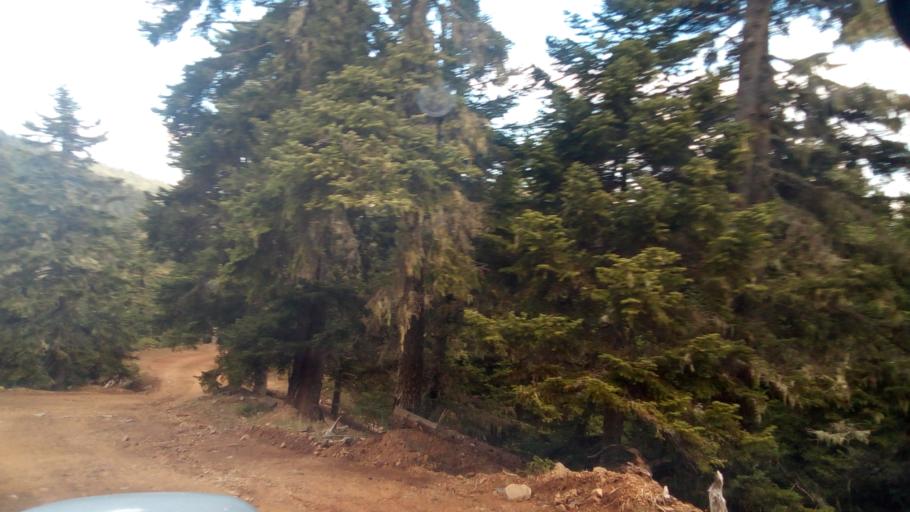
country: GR
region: Central Greece
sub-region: Nomos Fokidos
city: Lidoriki
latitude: 38.6123
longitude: 21.9721
